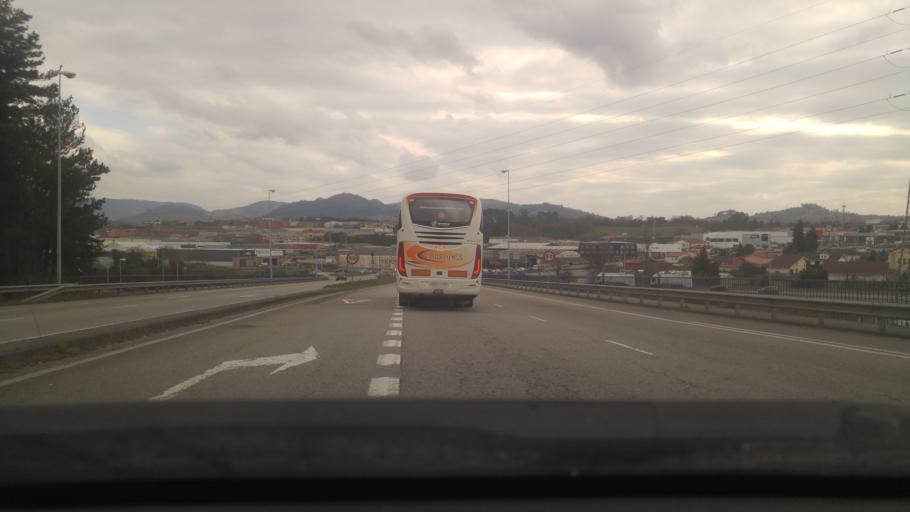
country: ES
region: Asturias
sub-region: Province of Asturias
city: Natahoyo
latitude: 43.5151
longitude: -5.6870
